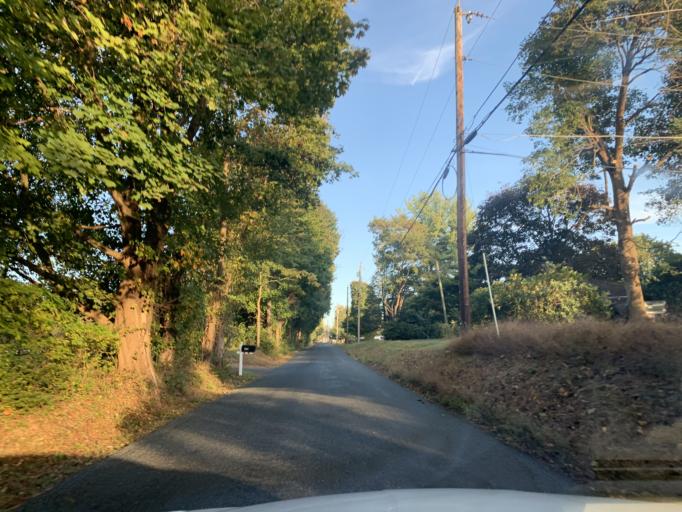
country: US
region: Maryland
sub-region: Harford County
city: Fallston
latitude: 39.5104
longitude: -76.4118
